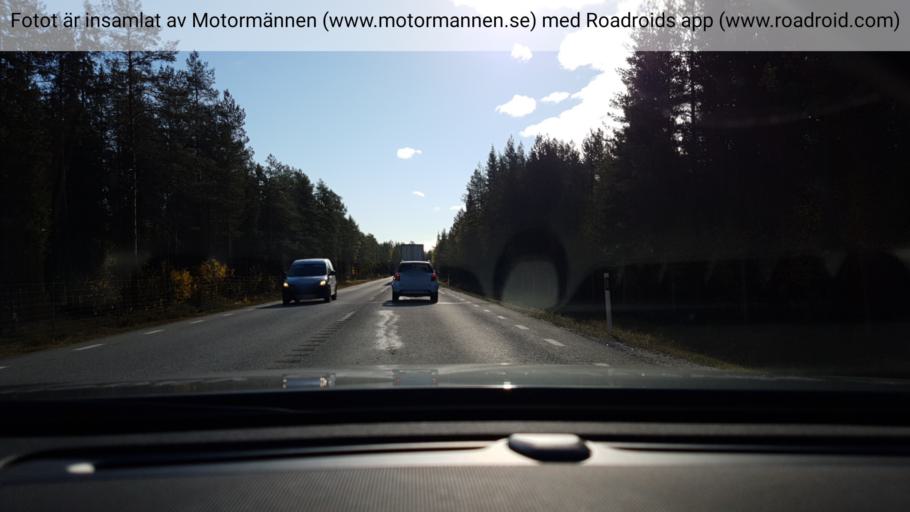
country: SE
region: Vaesterbotten
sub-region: Skelleftea Kommun
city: Burea
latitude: 64.4831
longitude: 21.2830
